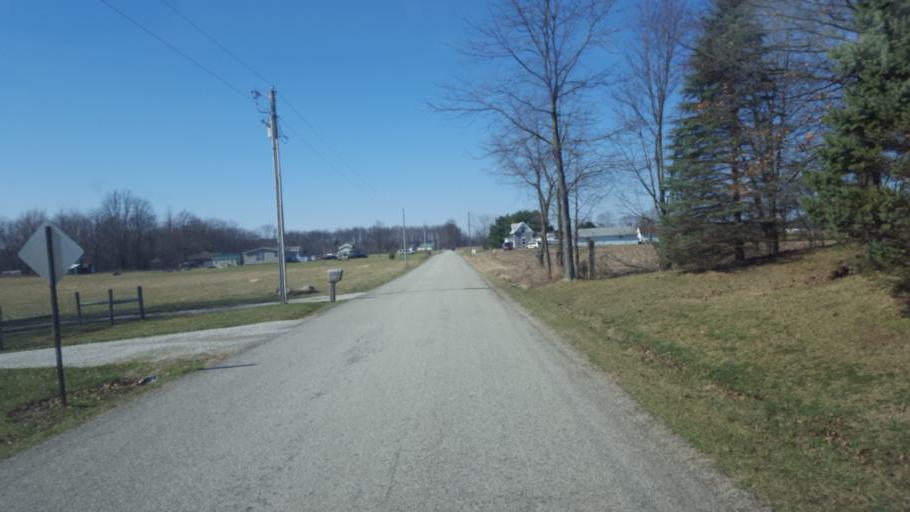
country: US
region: Ohio
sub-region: Morrow County
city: Cardington
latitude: 40.4991
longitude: -82.9241
